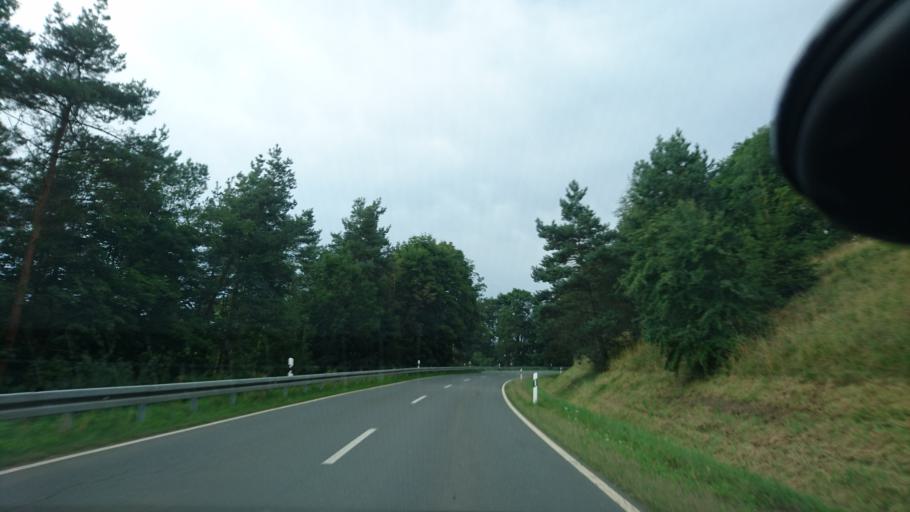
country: DE
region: Bavaria
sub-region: Upper Franconia
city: Selbitz
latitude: 50.3069
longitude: 11.7461
